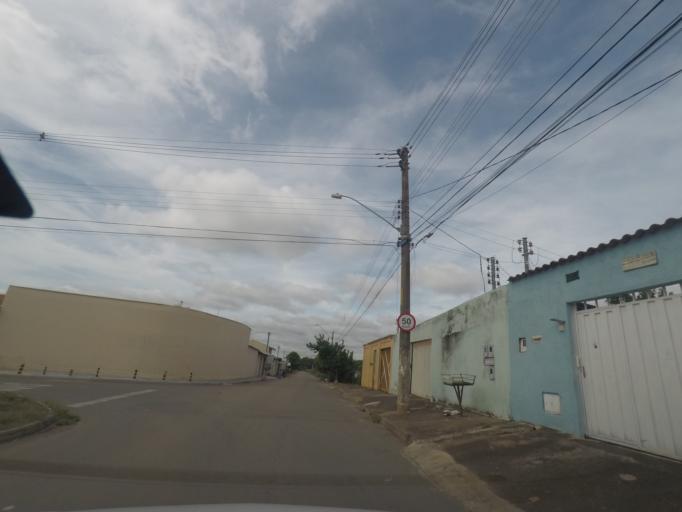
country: BR
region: Goias
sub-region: Goiania
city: Goiania
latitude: -16.6699
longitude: -49.1843
